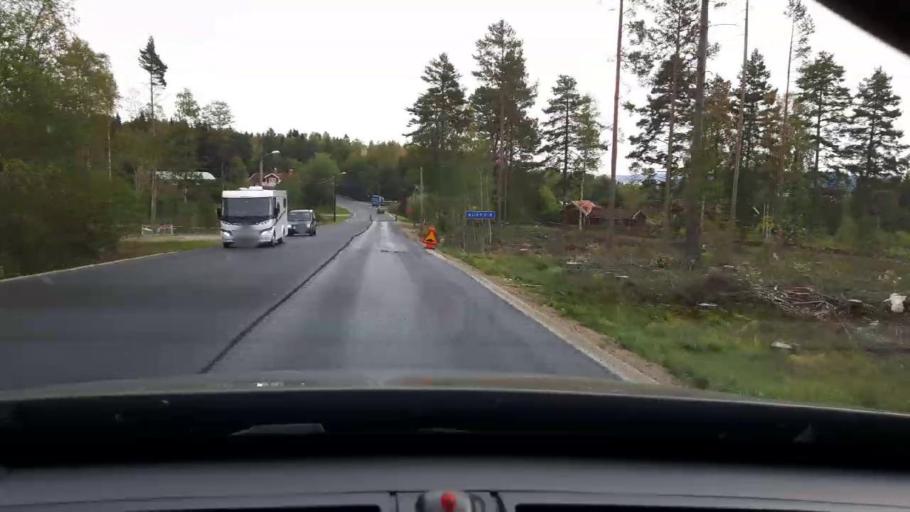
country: SE
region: Dalarna
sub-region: Ludvika Kommun
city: Ludvika
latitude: 60.2127
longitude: 15.1047
